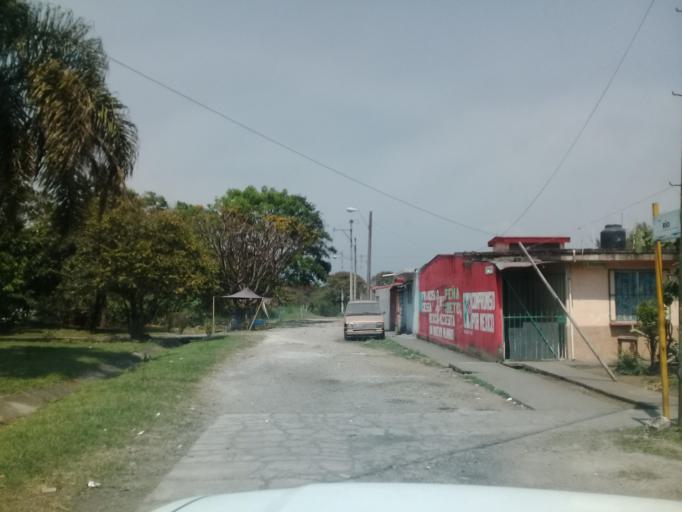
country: MX
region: Veracruz
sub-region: Ixtaczoquitlan
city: Buenavista
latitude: 18.8770
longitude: -97.0509
